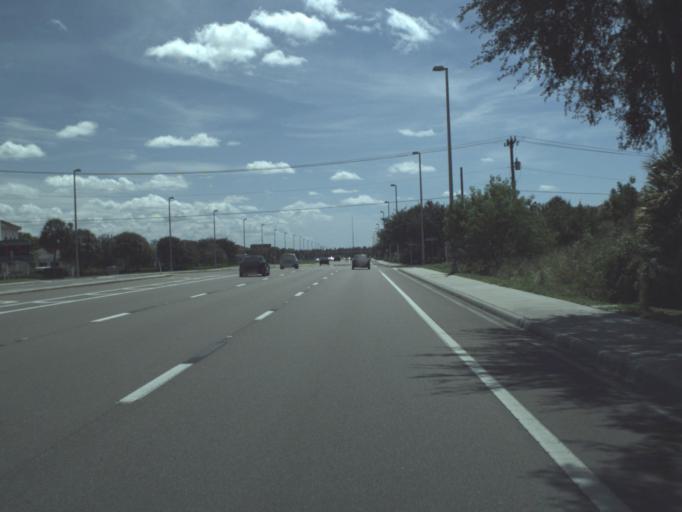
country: US
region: Florida
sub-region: Lee County
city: Villas
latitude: 26.5365
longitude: -81.8529
